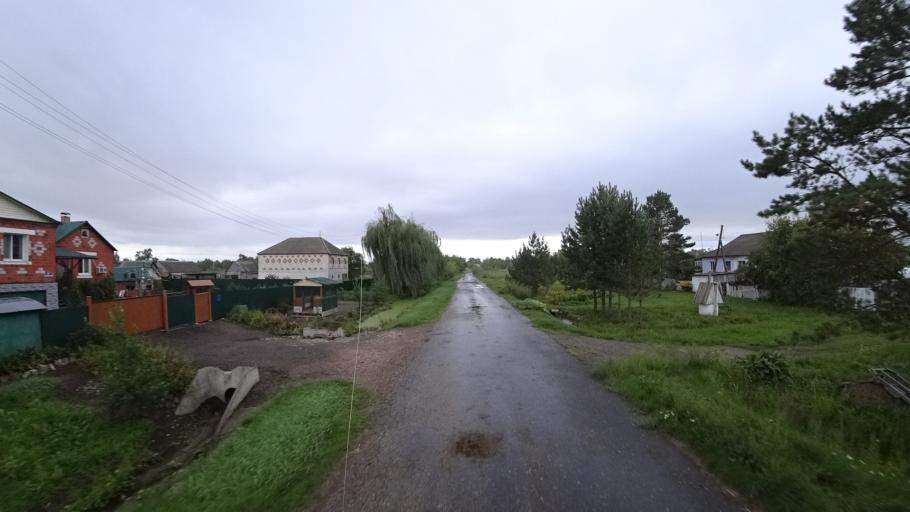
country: RU
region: Primorskiy
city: Chernigovka
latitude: 44.4076
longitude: 132.5324
